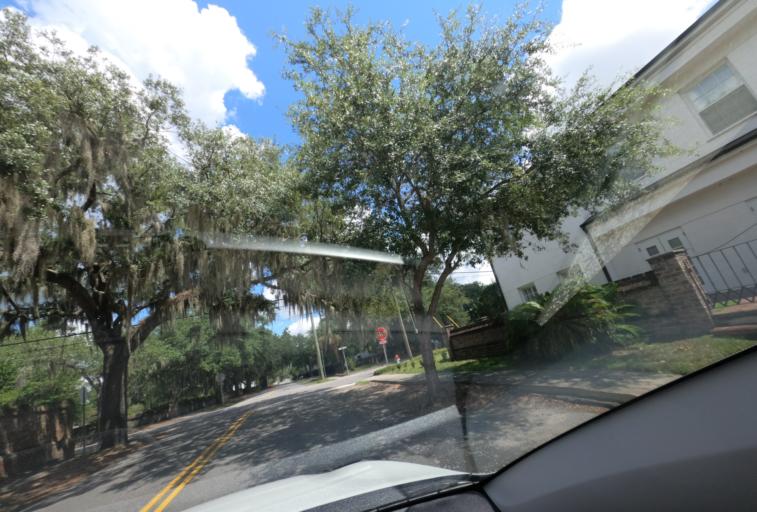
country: US
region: South Carolina
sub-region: Beaufort County
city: Beaufort
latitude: 32.4340
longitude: -80.6740
